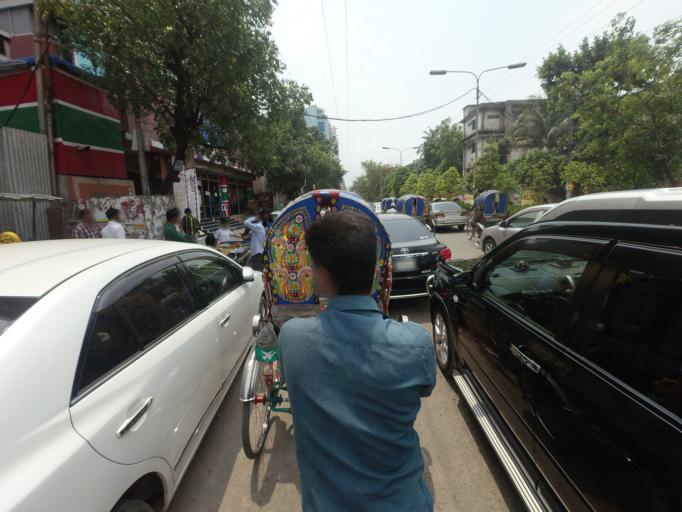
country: BD
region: Dhaka
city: Azimpur
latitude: 23.7547
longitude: 90.3645
